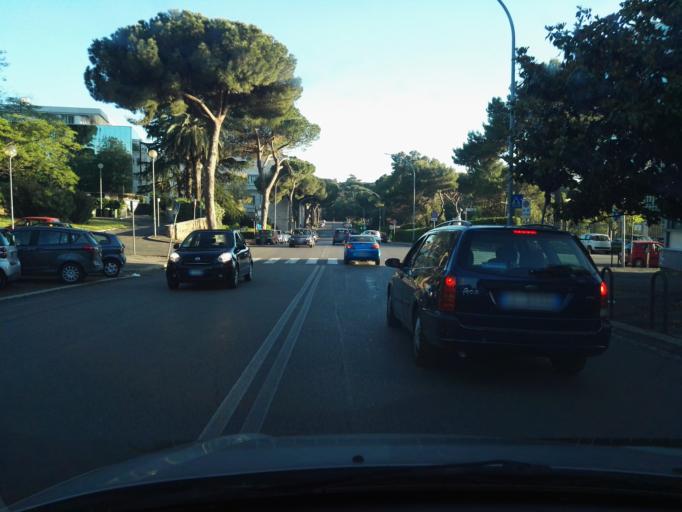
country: IT
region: Latium
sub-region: Citta metropolitana di Roma Capitale
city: Selcetta
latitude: 41.8285
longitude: 12.4738
